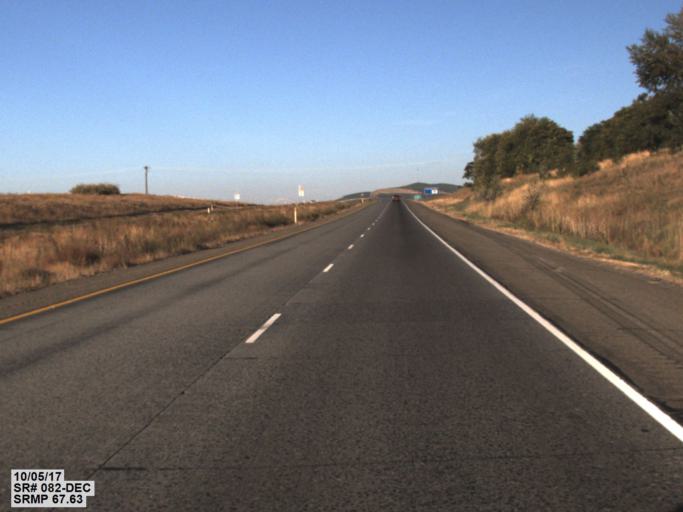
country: US
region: Washington
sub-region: Yakima County
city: Sunnyside
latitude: 46.3062
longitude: -120.0058
